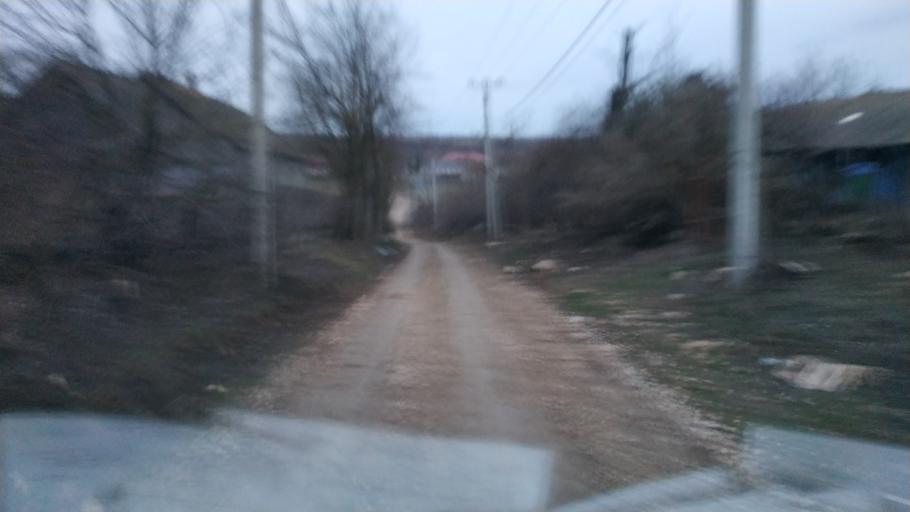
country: MD
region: Causeni
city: Causeni
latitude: 46.5001
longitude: 29.4076
